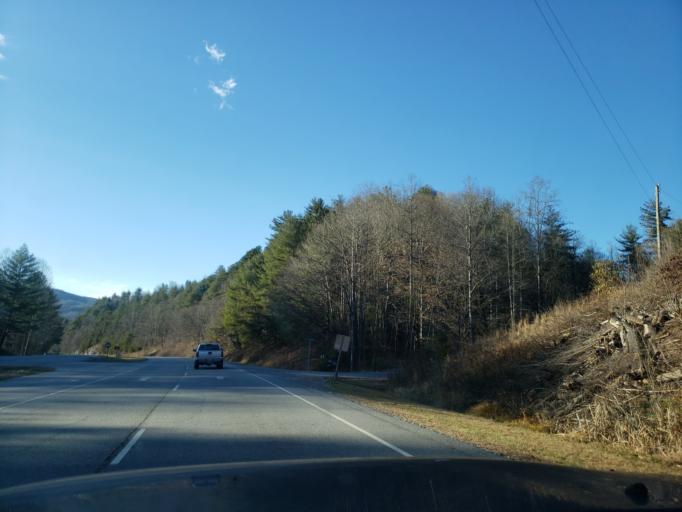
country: US
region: North Carolina
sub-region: Wilkes County
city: Millers Creek
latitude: 36.1805
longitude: -81.3856
